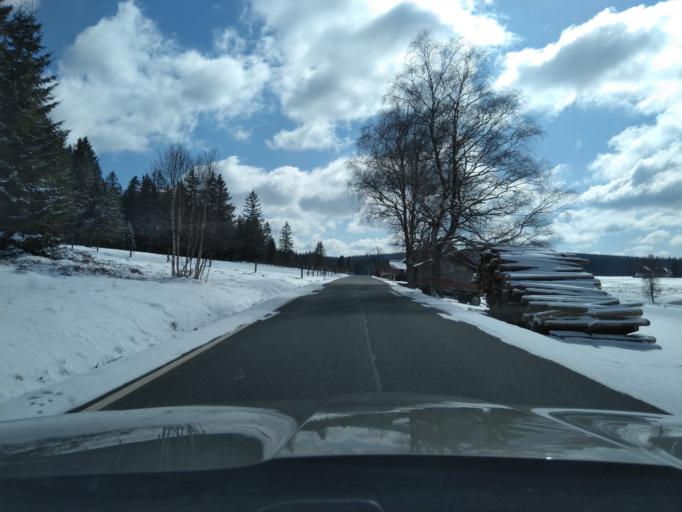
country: CZ
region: Plzensky
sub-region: Okres Klatovy
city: Kasperske Hory
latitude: 49.0501
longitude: 13.5750
